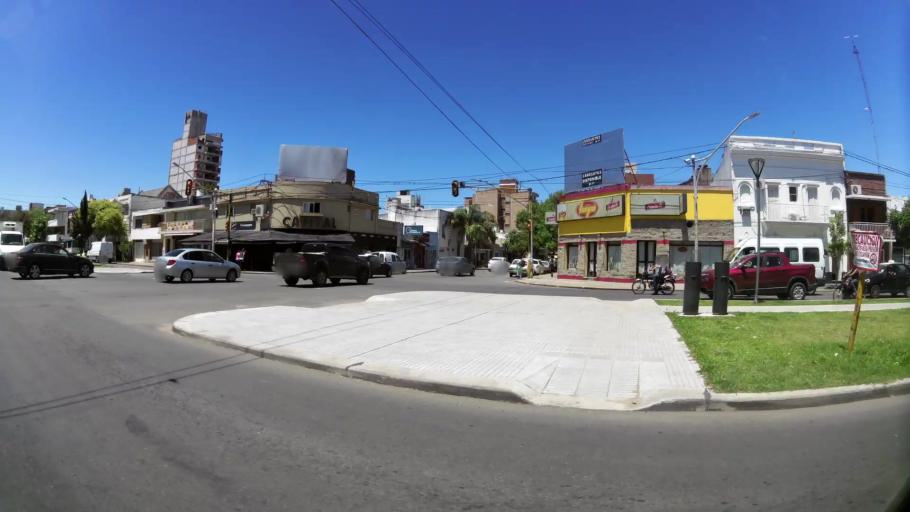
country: AR
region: Santa Fe
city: Santa Fe de la Vera Cruz
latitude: -31.6341
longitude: -60.7103
